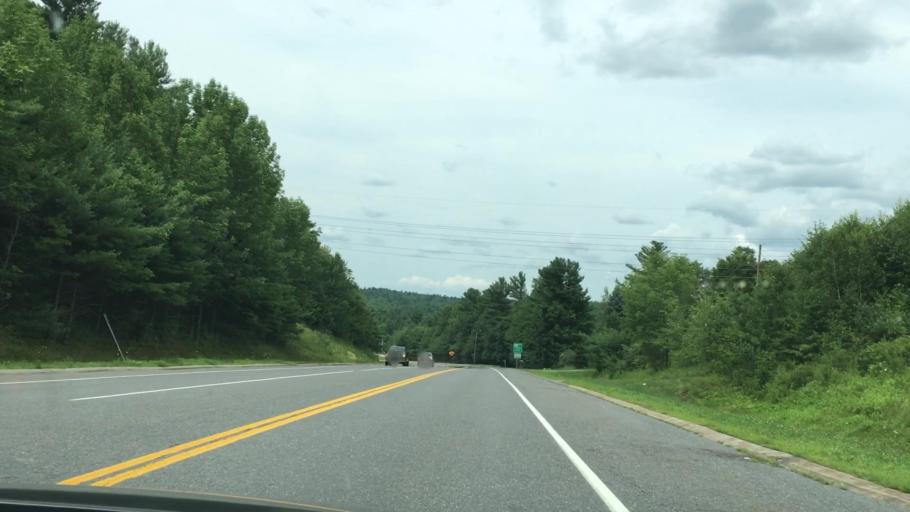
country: US
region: Massachusetts
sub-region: Worcester County
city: Gardner
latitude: 42.6000
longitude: -71.9884
